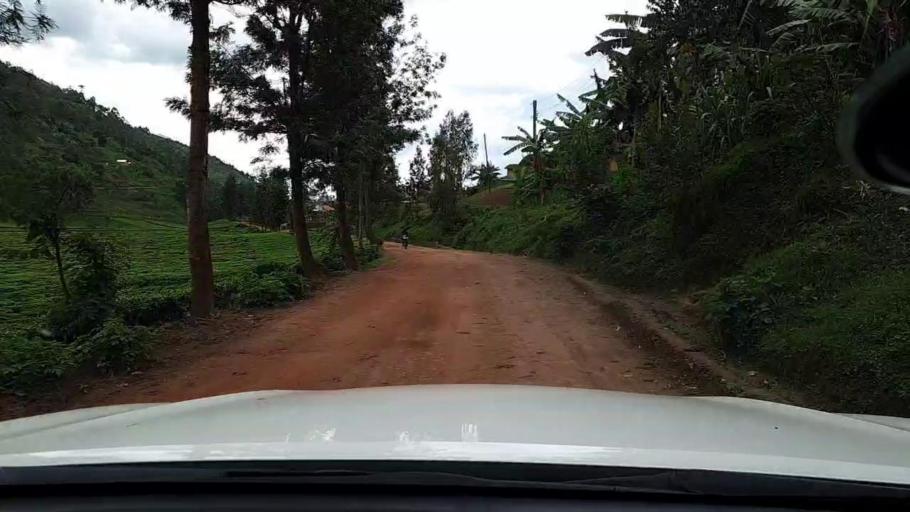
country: RW
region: Northern Province
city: Byumba
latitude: -1.6568
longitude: 29.9093
